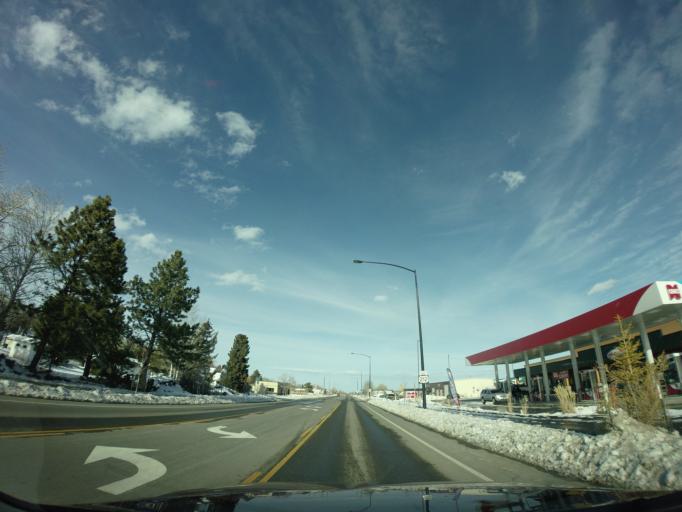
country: US
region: Montana
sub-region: Carbon County
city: Red Lodge
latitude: 45.1960
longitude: -109.2467
